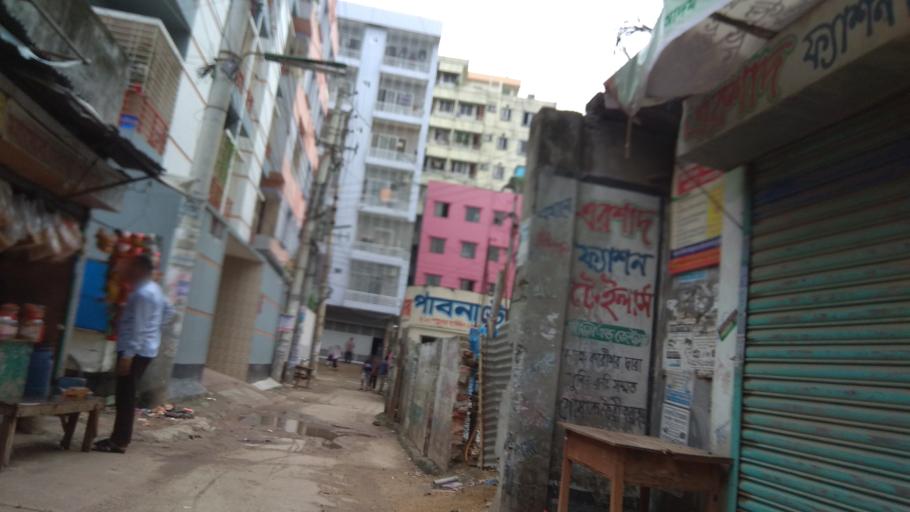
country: BD
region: Dhaka
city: Azimpur
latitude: 23.7996
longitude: 90.3623
